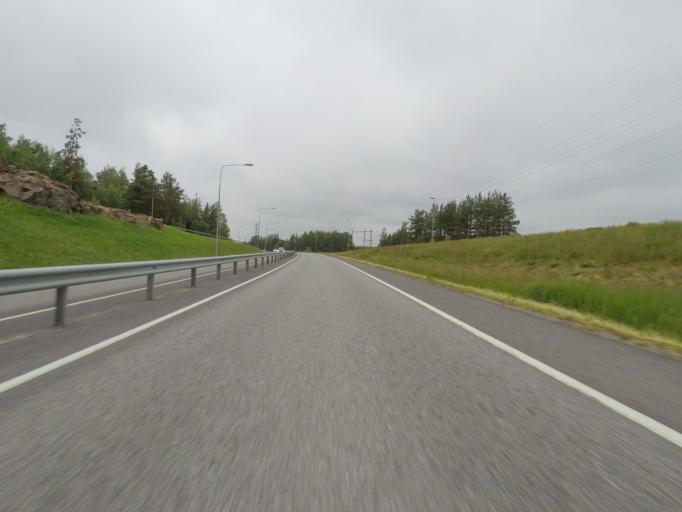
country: FI
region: Varsinais-Suomi
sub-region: Turku
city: Naantali
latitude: 60.4744
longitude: 22.0665
